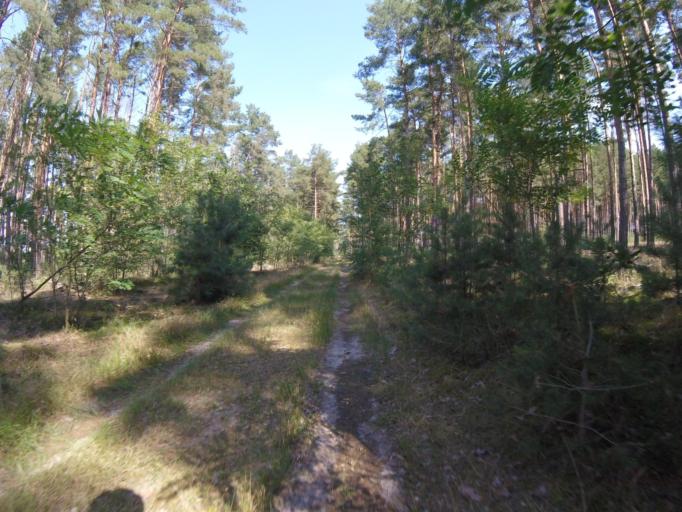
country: DE
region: Brandenburg
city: Bestensee
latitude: 52.2202
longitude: 13.6958
